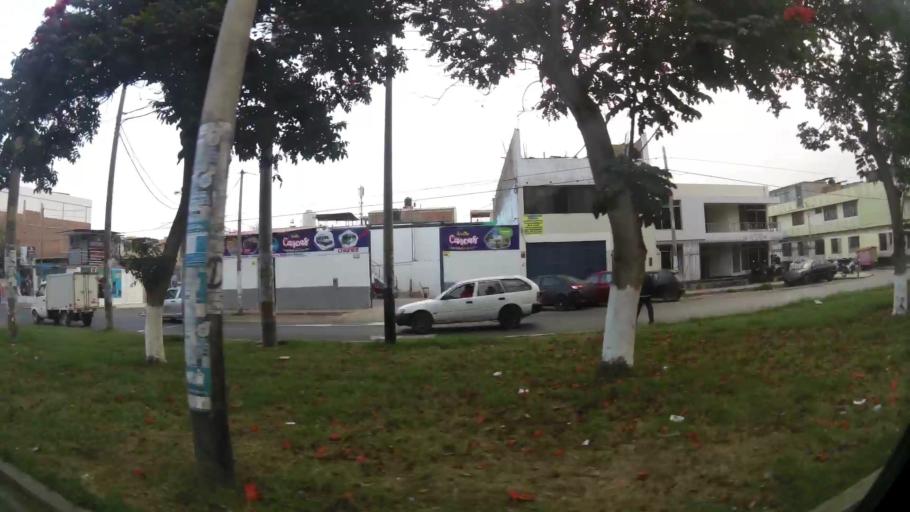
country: PE
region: La Libertad
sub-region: Provincia de Trujillo
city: Trujillo
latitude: -8.0960
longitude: -79.0312
